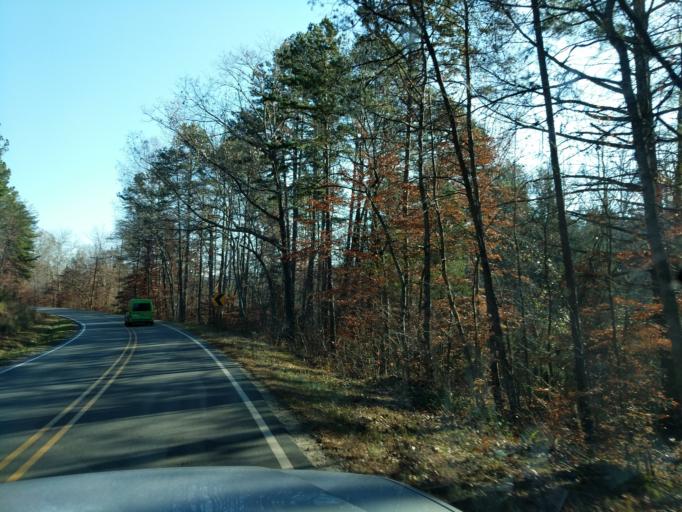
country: US
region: North Carolina
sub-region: Rutherford County
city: Rutherfordton
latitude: 35.2795
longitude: -82.0327
